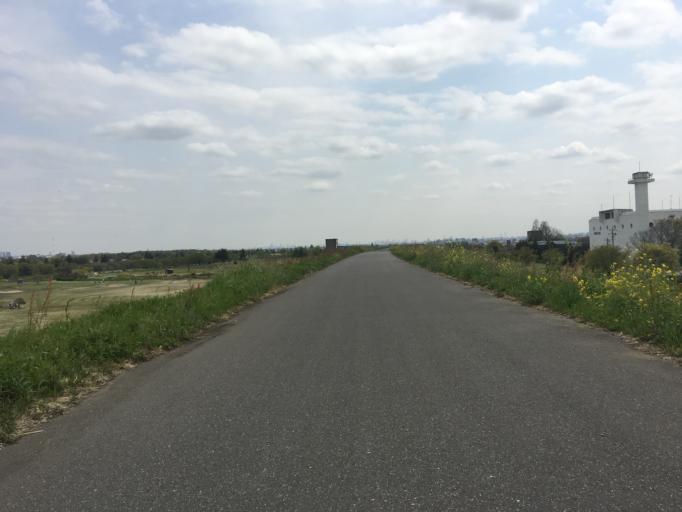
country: JP
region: Saitama
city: Shiki
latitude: 35.8738
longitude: 139.5719
